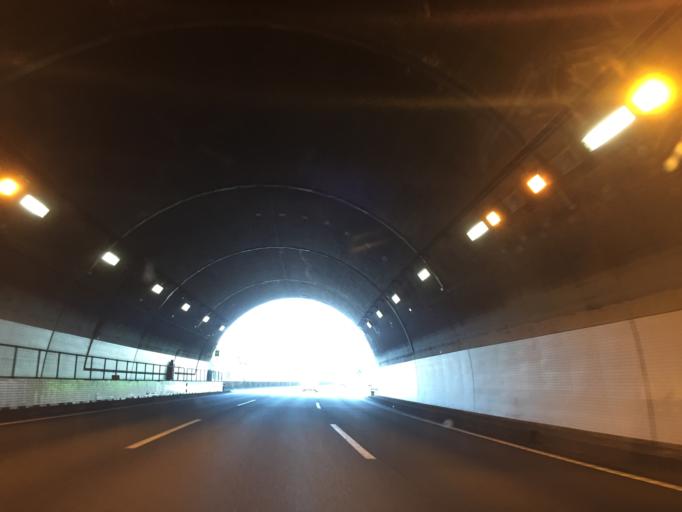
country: JP
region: Shizuoka
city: Gotemba
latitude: 35.3513
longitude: 138.9840
